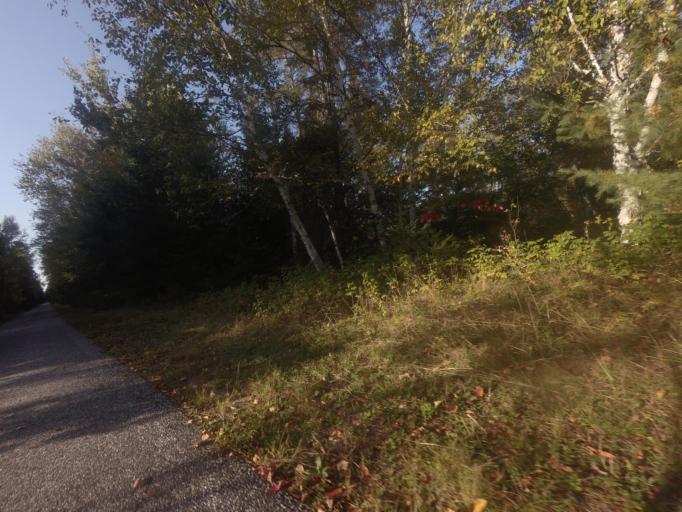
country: CA
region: Quebec
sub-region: Laurentides
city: Riviere-Rouge
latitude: 46.4338
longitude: -74.8963
